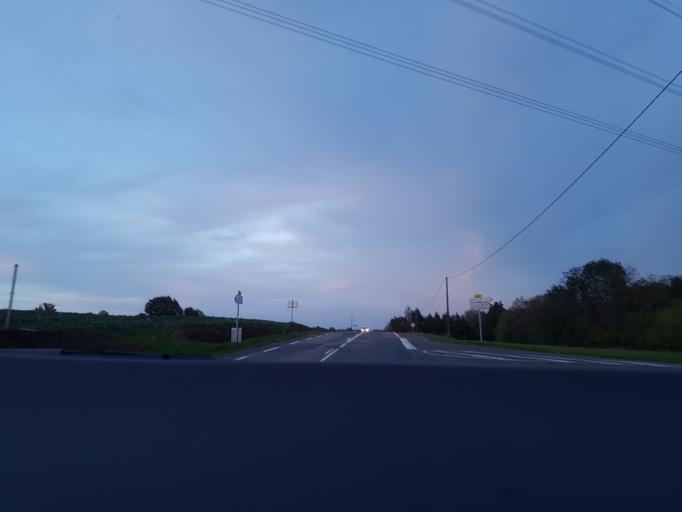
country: FR
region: Pays de la Loire
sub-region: Departement de la Mayenne
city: Cosse-le-Vivien
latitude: 47.9577
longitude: -0.8976
